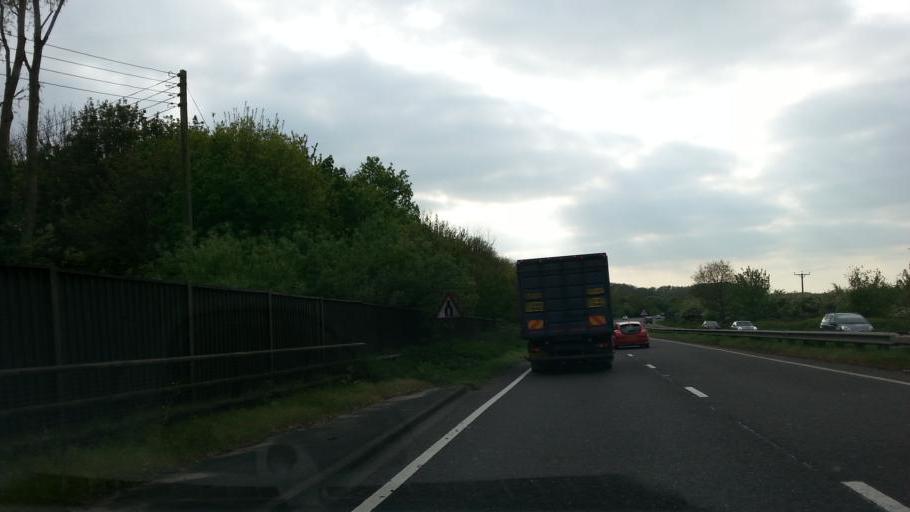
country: GB
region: England
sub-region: Nottinghamshire
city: South Collingham
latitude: 53.0762
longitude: -0.6972
